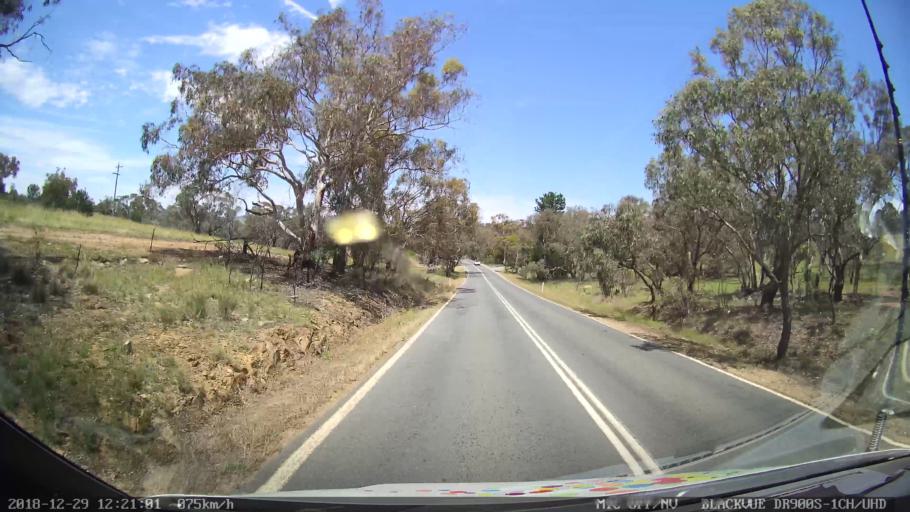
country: AU
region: New South Wales
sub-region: Queanbeyan
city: Queanbeyan
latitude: -35.4091
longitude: 149.2261
